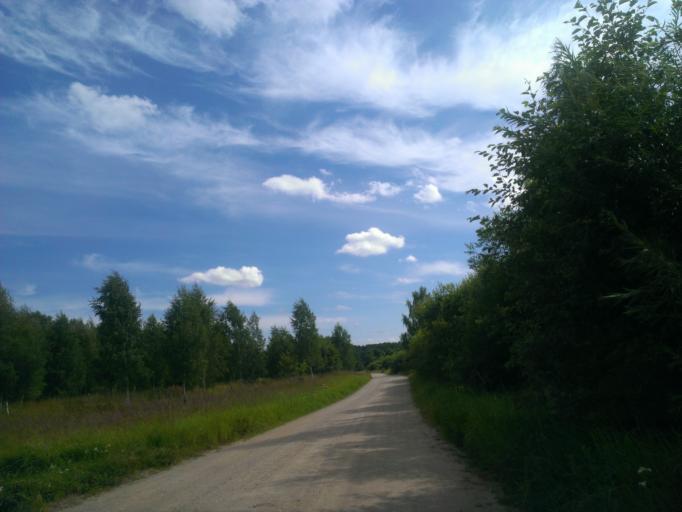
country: LV
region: Ligatne
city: Ligatne
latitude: 57.2185
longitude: 25.0097
